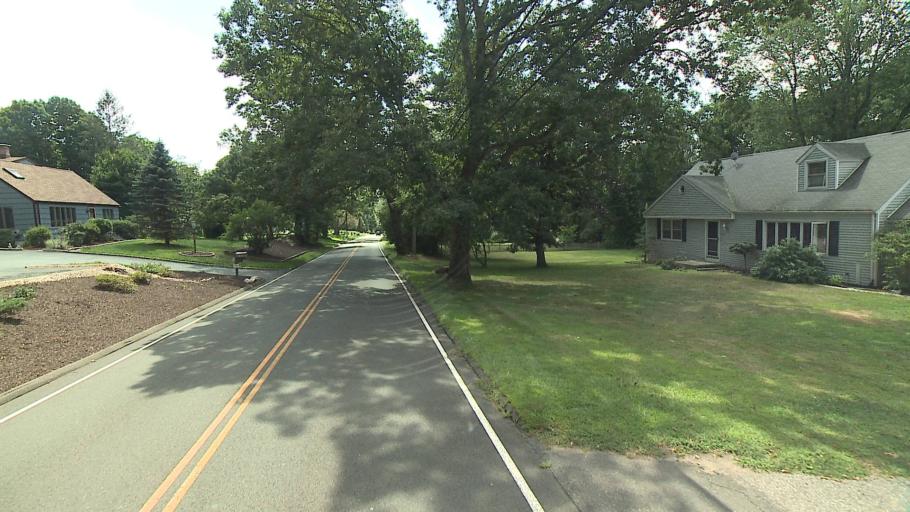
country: US
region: Connecticut
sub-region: Fairfield County
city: Trumbull
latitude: 41.2783
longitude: -73.1594
